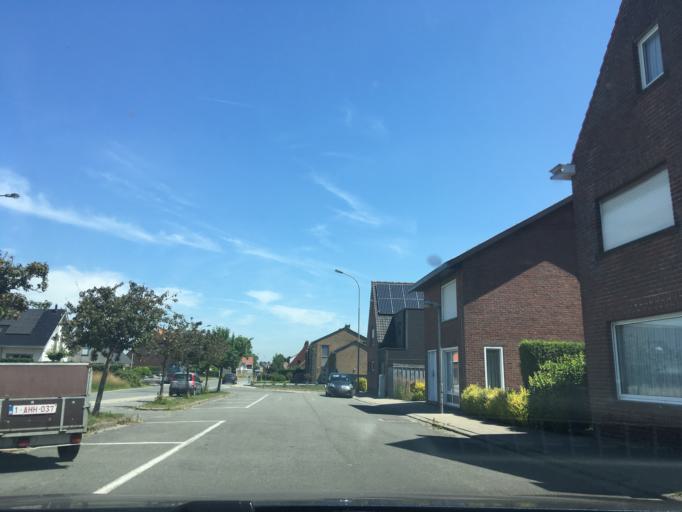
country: BE
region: Flanders
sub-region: Provincie West-Vlaanderen
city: Tielt
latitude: 51.0031
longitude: 3.3119
